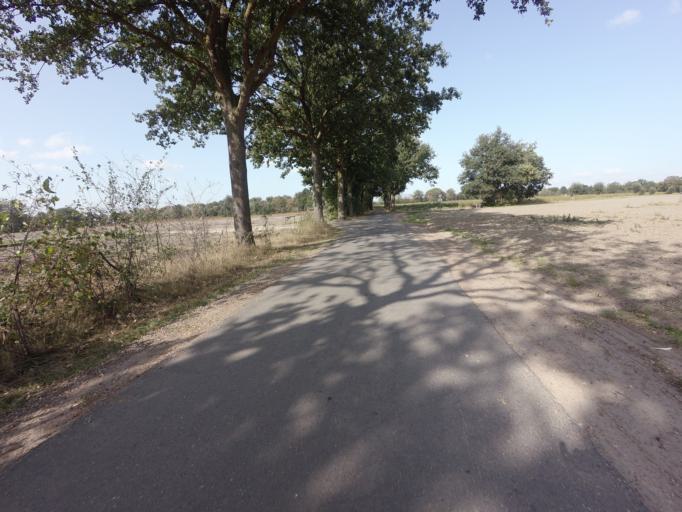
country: NL
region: Limburg
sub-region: Gemeente Roerdalen
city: Herkenbosch
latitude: 51.1927
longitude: 6.0594
